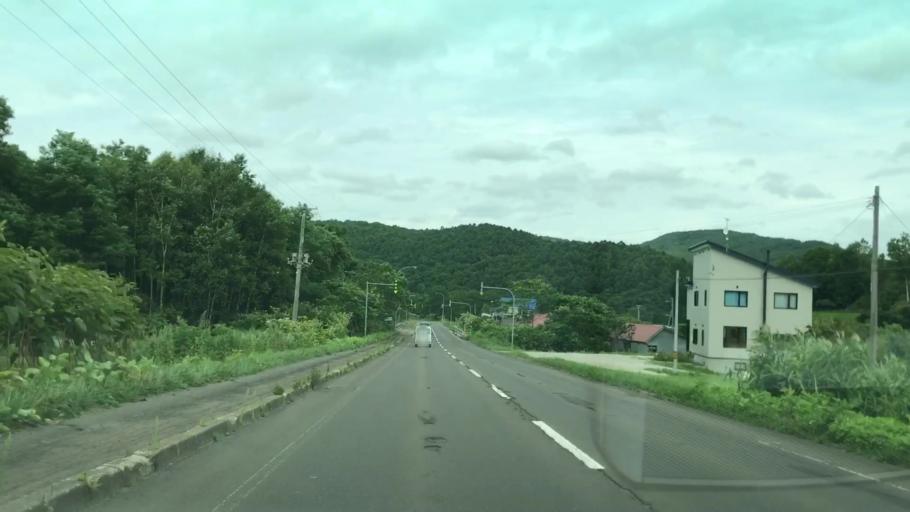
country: JP
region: Hokkaido
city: Niseko Town
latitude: 42.9613
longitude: 140.6934
